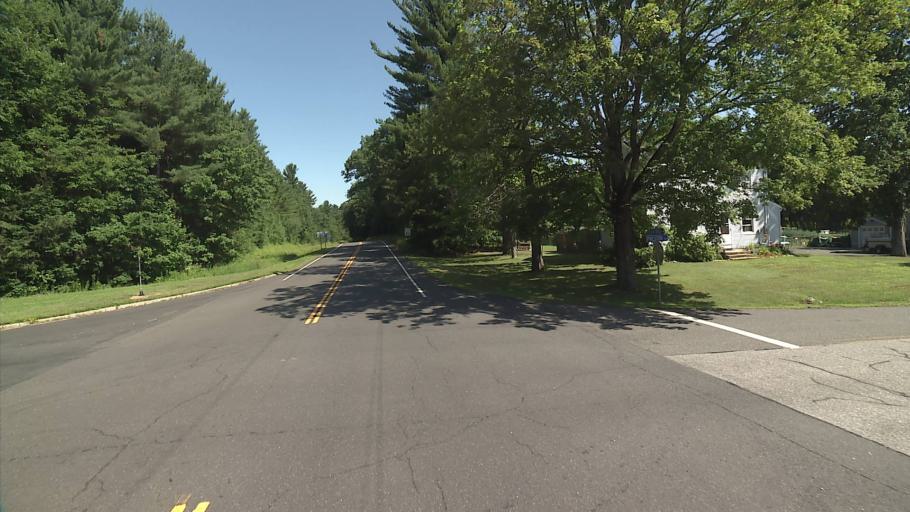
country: US
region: Connecticut
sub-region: Litchfield County
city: Terryville
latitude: 41.7016
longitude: -73.0079
